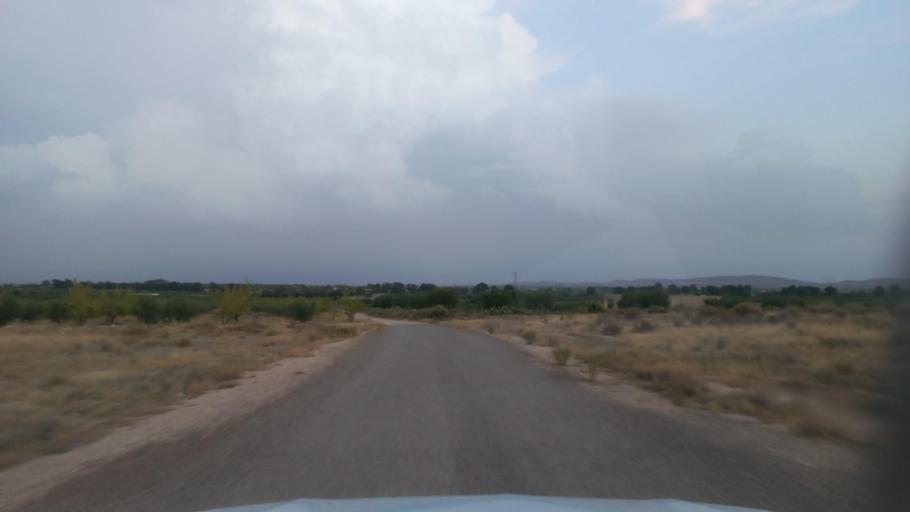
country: TN
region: Al Qasrayn
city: Kasserine
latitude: 35.2686
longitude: 9.0356
